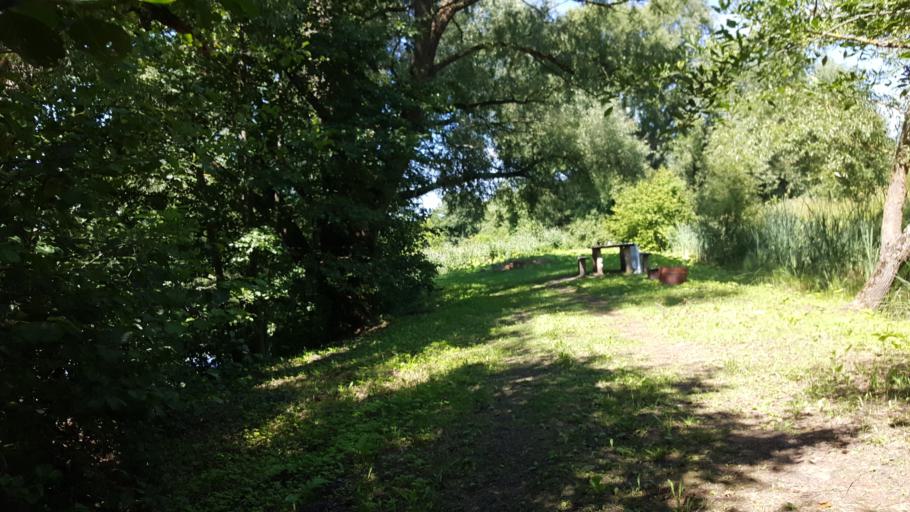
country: BY
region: Brest
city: Charnawchytsy
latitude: 52.3580
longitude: 23.6196
